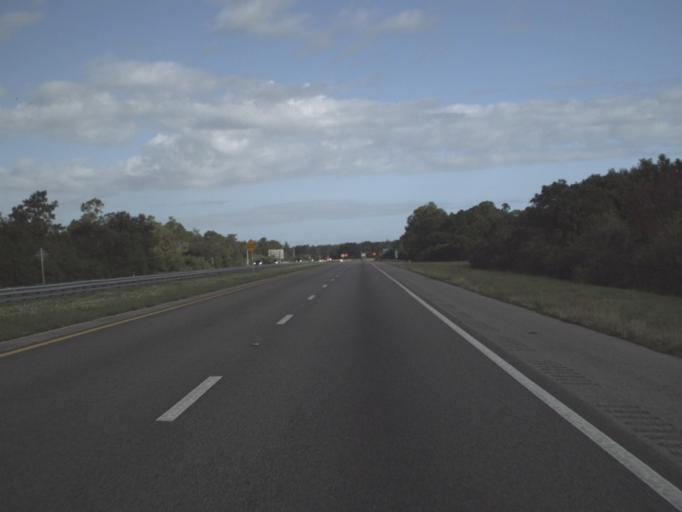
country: US
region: Florida
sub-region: Osceola County
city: Saint Cloud
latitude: 28.2024
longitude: -81.3064
